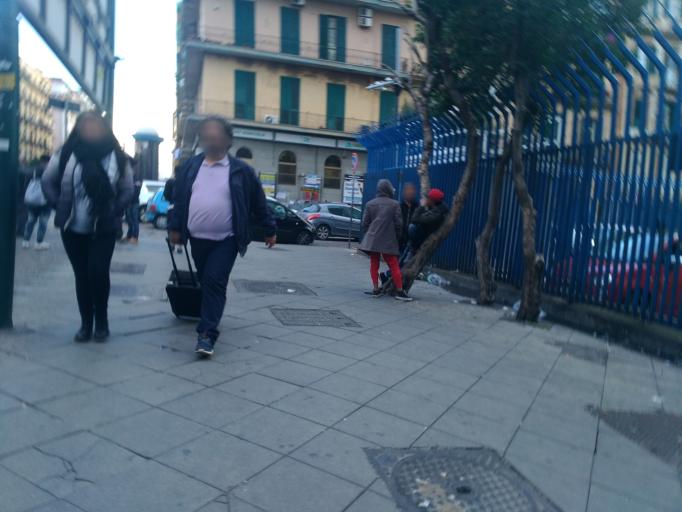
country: IT
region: Campania
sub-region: Provincia di Napoli
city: Napoli
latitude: 40.8540
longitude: 14.2716
